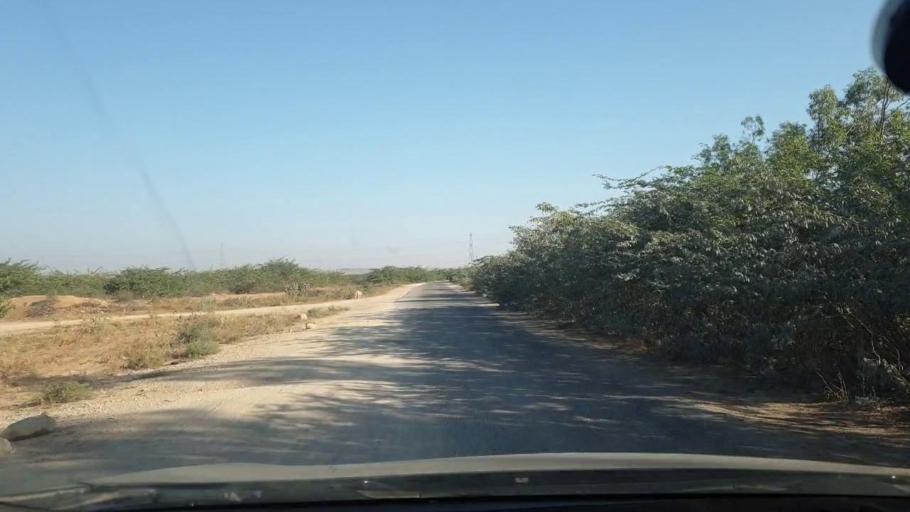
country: PK
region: Sindh
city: Malir Cantonment
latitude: 25.1542
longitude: 67.1909
